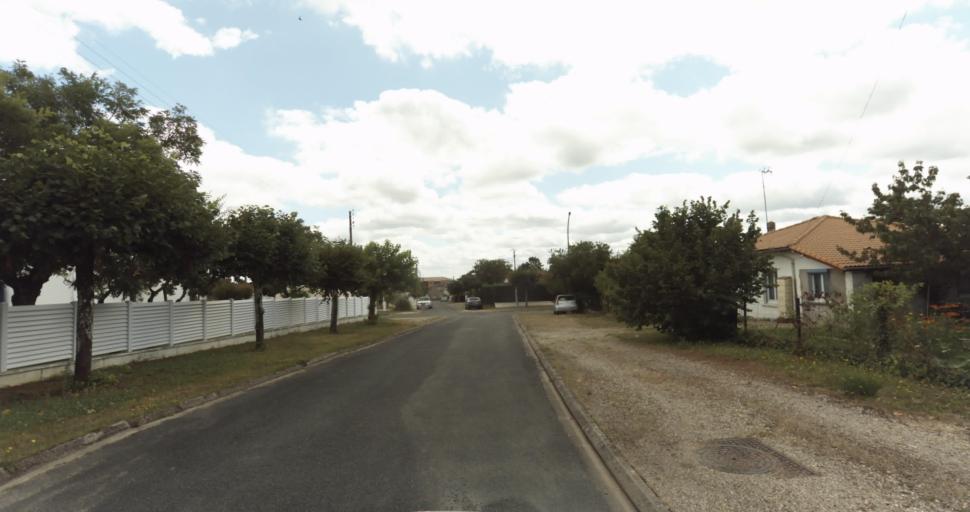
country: FR
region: Aquitaine
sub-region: Departement de la Gironde
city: Bazas
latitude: 44.4365
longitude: -0.2206
